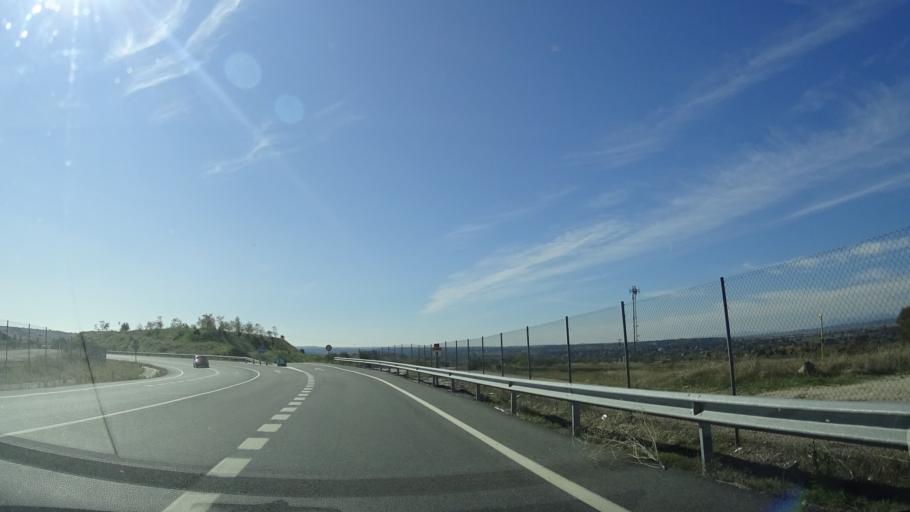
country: ES
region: Madrid
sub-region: Provincia de Madrid
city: Villanueva del Pardillo
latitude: 40.4849
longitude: -3.9225
